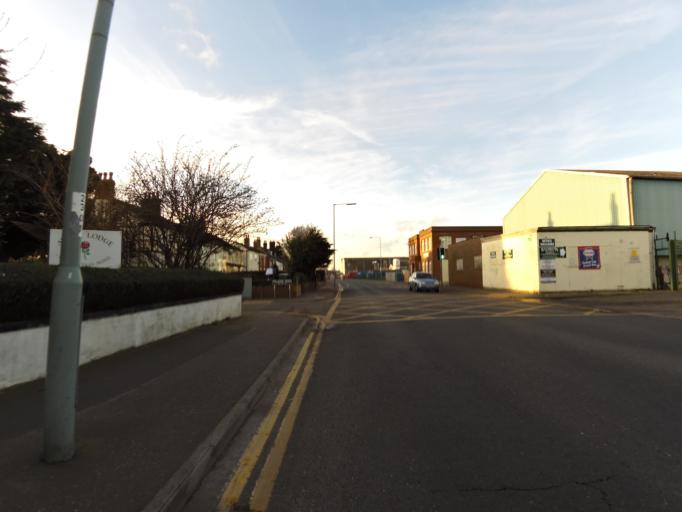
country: GB
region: England
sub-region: Norfolk
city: Great Yarmouth
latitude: 52.5968
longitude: 1.7252
